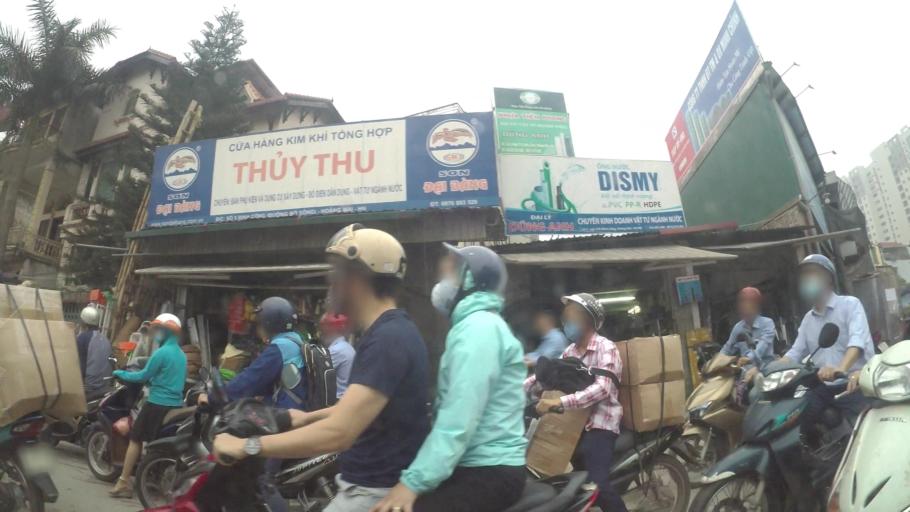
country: VN
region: Ha Noi
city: Hai BaTrung
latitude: 20.9834
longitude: 105.8345
